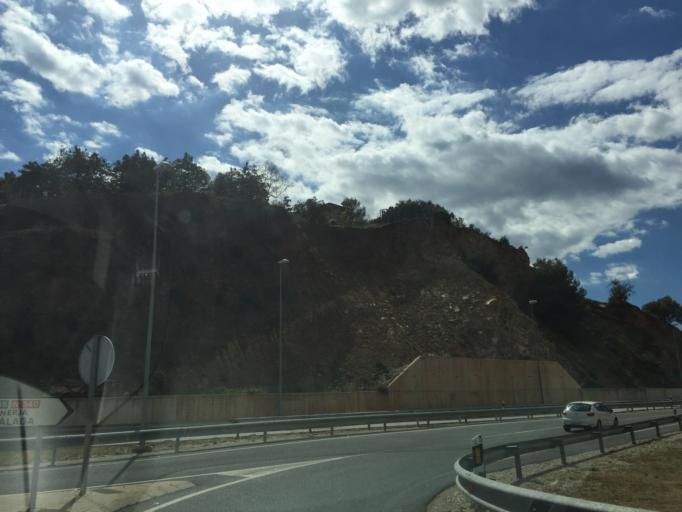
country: ES
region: Andalusia
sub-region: Provincia de Granada
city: La Herradura
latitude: 36.7506
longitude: -3.7832
